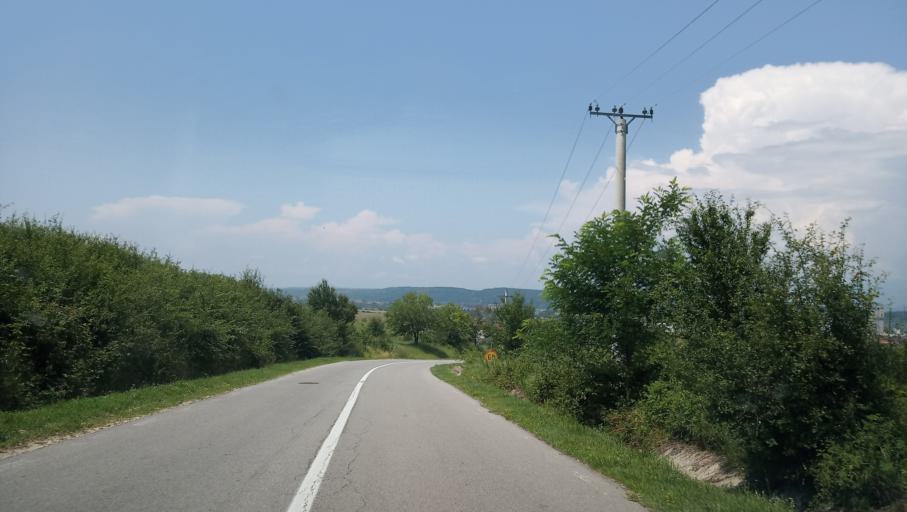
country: RO
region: Gorj
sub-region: Comuna Turcinesti
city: Turcinesti
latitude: 45.0639
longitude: 23.3274
